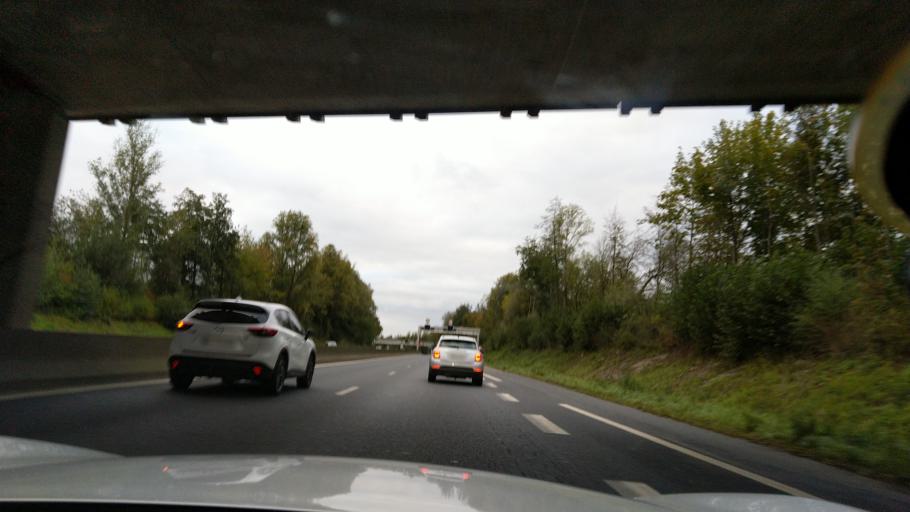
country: FR
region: Haute-Normandie
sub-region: Departement de la Seine-Maritime
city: Bois-Guillaume
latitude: 49.4748
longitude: 1.1359
